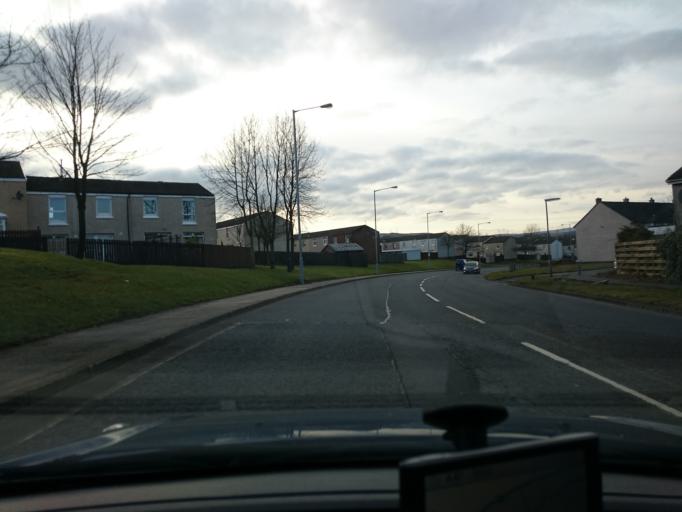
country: GB
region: Scotland
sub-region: Falkirk
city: Denny
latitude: 56.0121
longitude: -3.9130
